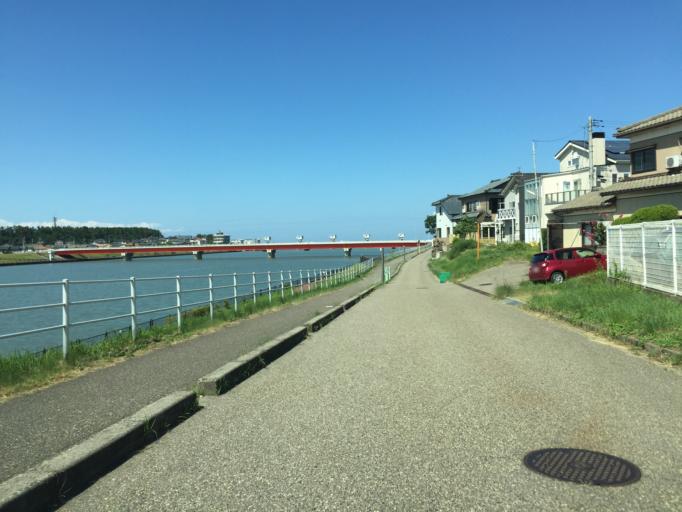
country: JP
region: Niigata
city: Niigata-shi
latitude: 37.9030
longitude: 139.0086
